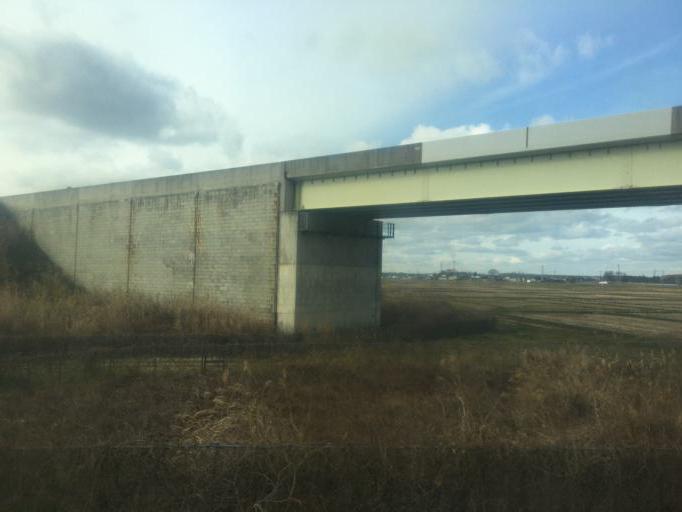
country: JP
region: Akita
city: Noshiromachi
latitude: 40.1771
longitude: 140.0586
